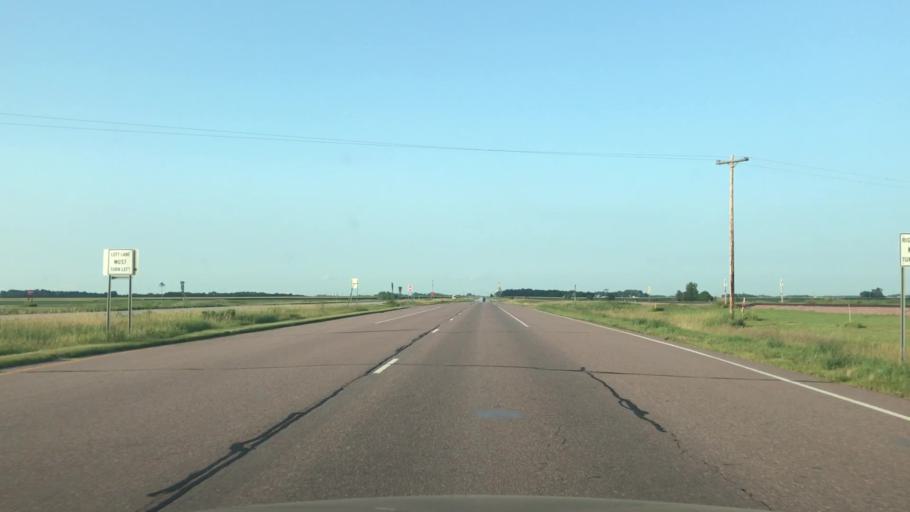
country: US
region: Minnesota
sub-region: Nobles County
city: Worthington
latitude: 43.7464
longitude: -95.3979
